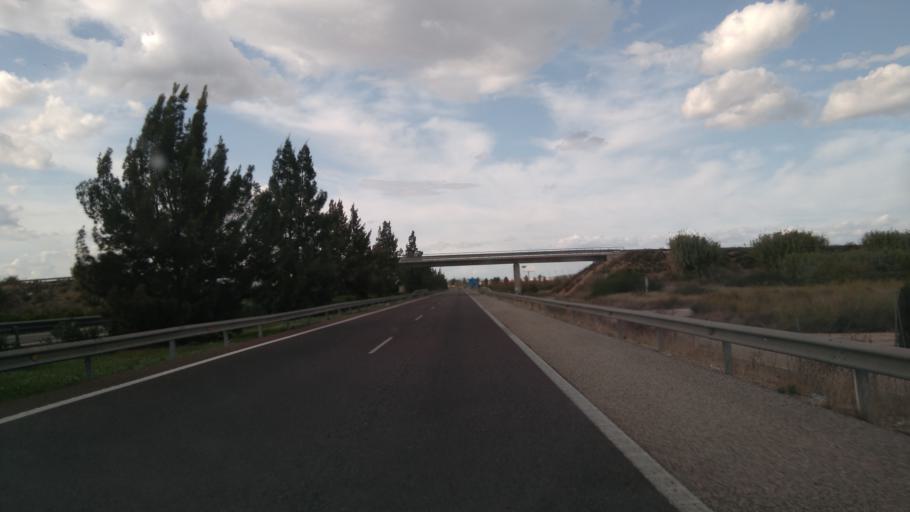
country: ES
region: Valencia
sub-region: Provincia de Valencia
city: Guadassuar
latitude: 39.1697
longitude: -0.4631
